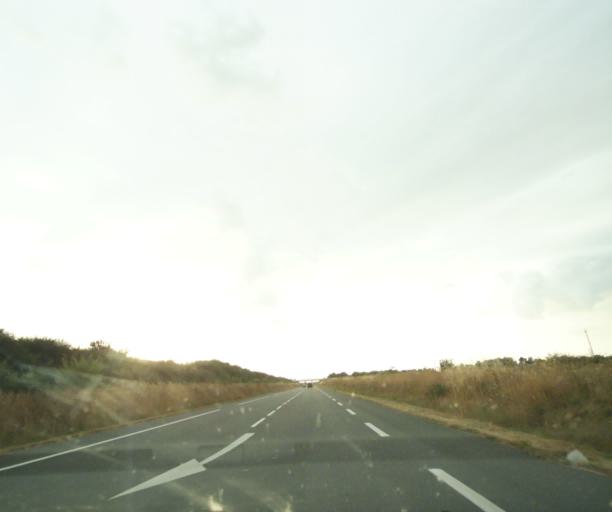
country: FR
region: Pays de la Loire
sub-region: Departement de la Vendee
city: Saint-Hilaire-de-Talmont
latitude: 46.4679
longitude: -1.6454
